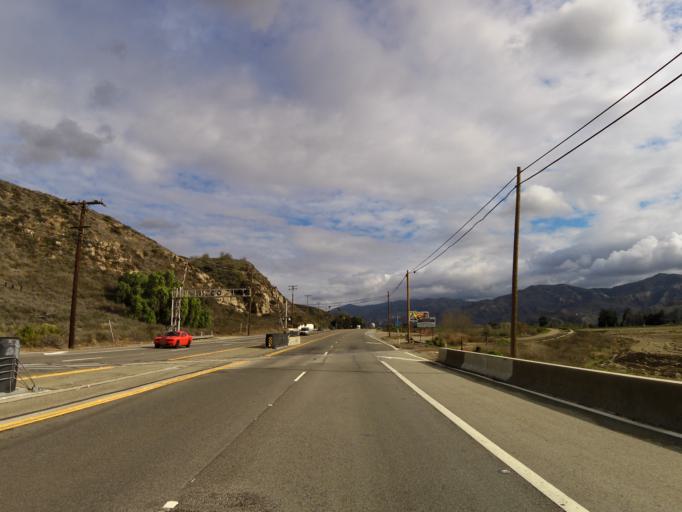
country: US
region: California
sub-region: Ventura County
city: Fillmore
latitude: 34.3980
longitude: -118.8948
